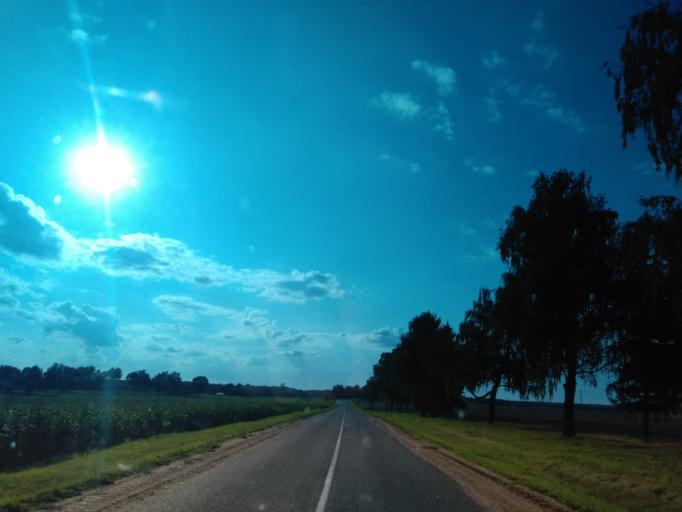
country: BY
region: Minsk
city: Kapyl'
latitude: 53.2041
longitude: 27.0382
